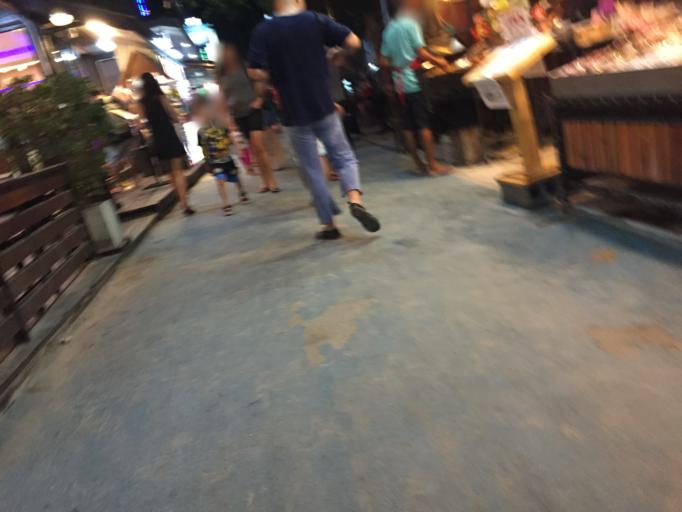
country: MY
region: Kedah
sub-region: Langkawi
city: Kuah
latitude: 6.4874
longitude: 99.3060
